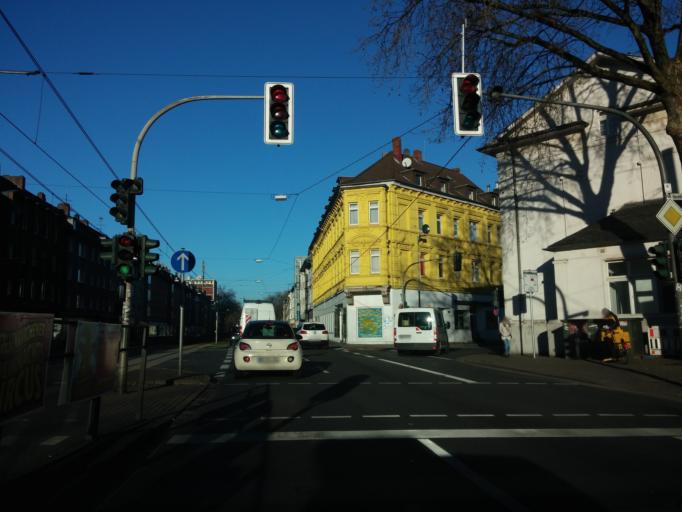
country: DE
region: North Rhine-Westphalia
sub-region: Regierungsbezirk Munster
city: Gelsenkirchen
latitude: 51.5286
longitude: 7.0840
